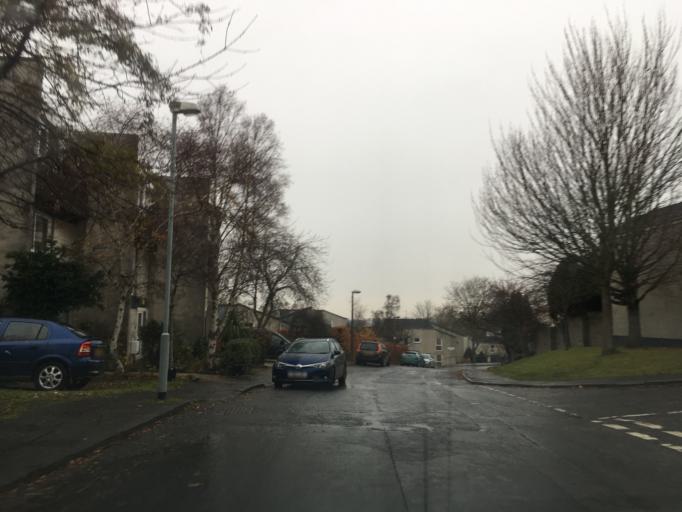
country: GB
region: Scotland
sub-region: Edinburgh
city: Currie
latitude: 55.9554
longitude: -3.3014
